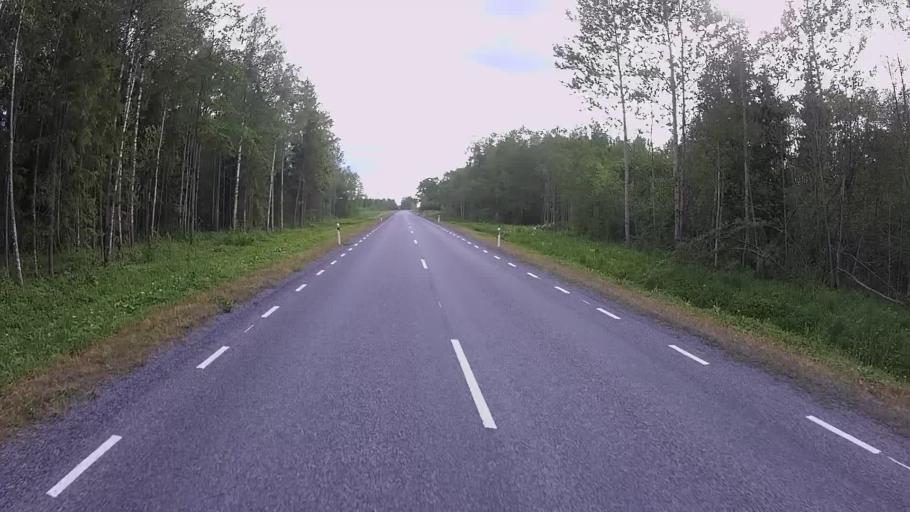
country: EE
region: Jogevamaa
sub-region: Mustvee linn
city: Mustvee
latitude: 59.0203
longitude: 26.9588
